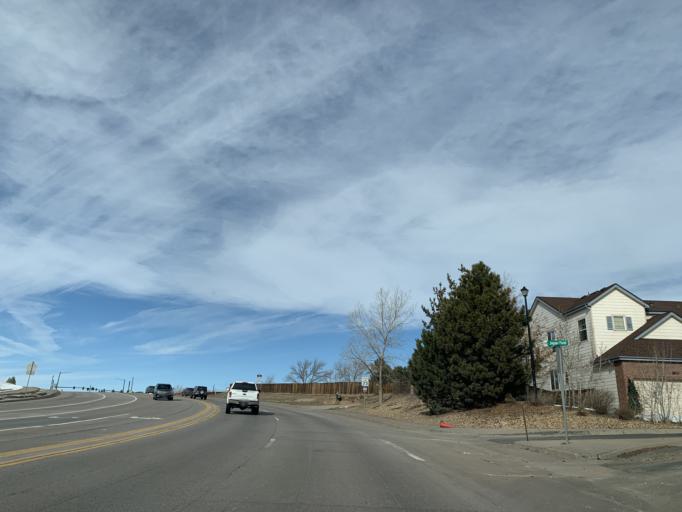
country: US
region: Colorado
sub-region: Douglas County
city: Carriage Club
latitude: 39.5216
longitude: -104.9180
